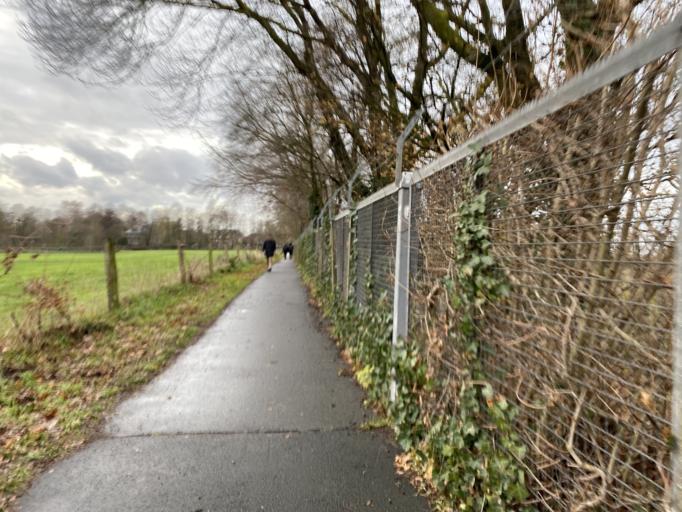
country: DE
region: North Rhine-Westphalia
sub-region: Regierungsbezirk Arnsberg
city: Hamm
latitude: 51.6811
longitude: 7.8416
